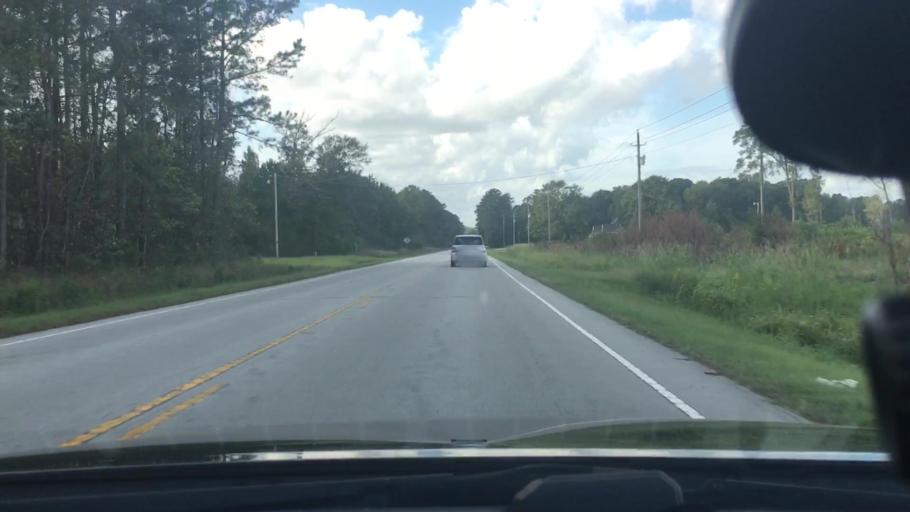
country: US
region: North Carolina
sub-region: Pitt County
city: Windsor
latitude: 35.4761
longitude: -77.2953
